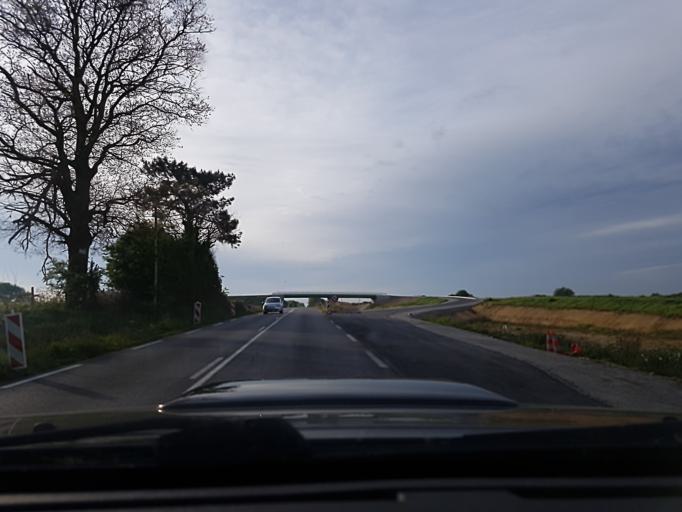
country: FR
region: Pays de la Loire
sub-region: Departement de la Vendee
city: Aizenay
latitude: 46.7587
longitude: -1.6443
